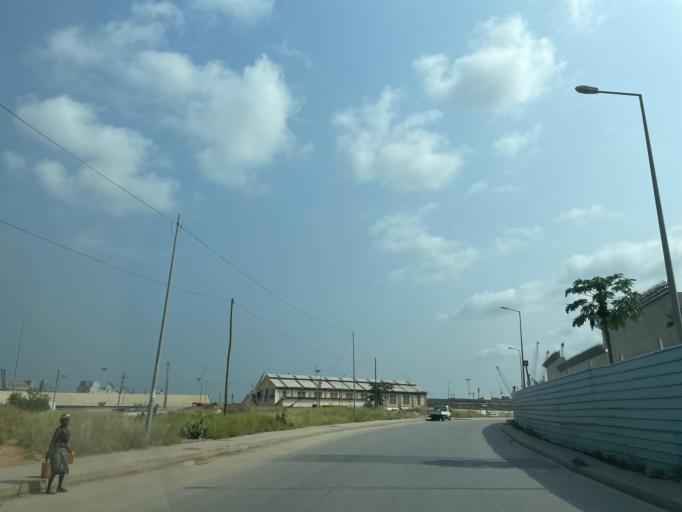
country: AO
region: Luanda
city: Luanda
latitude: -8.8047
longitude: 13.2468
